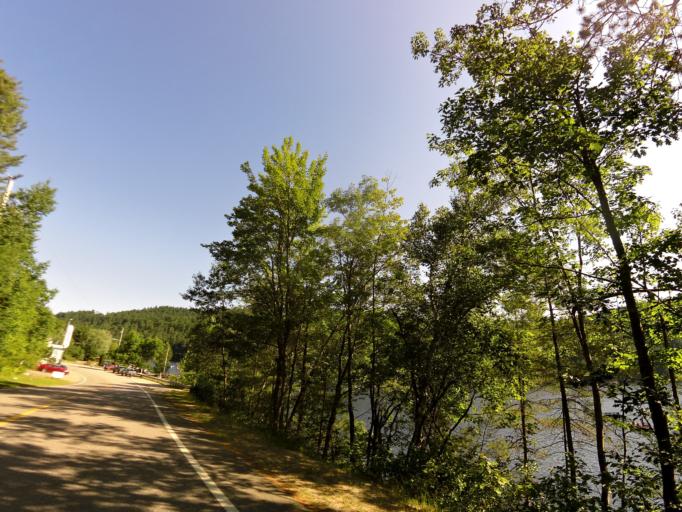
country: CA
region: Ontario
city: Deep River
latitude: 46.1983
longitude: -77.6835
